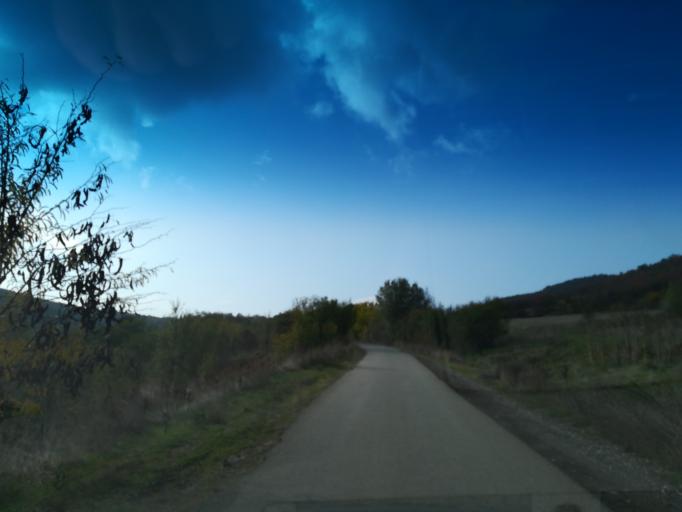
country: BG
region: Stara Zagora
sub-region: Obshtina Nikolaevo
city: Elkhovo
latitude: 42.3356
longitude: 25.4059
